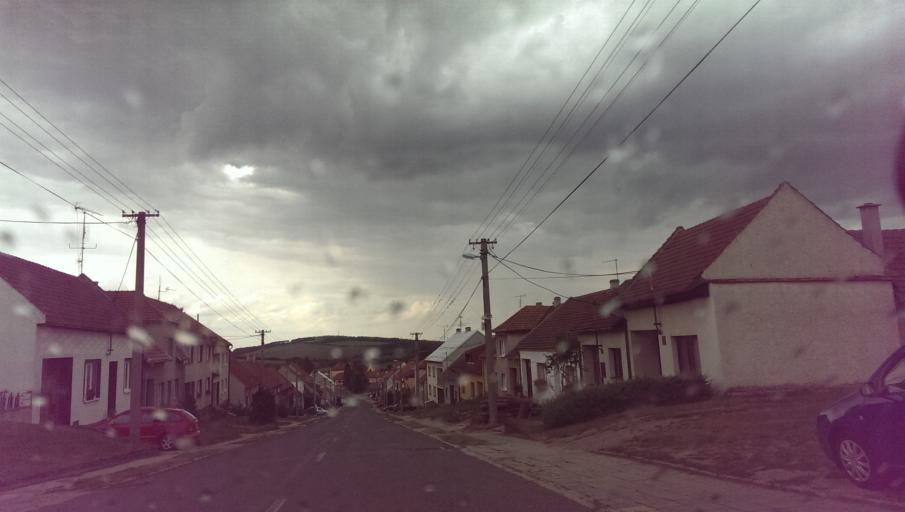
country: CZ
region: South Moravian
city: Velka nad Velickou
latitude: 48.9096
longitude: 17.5628
